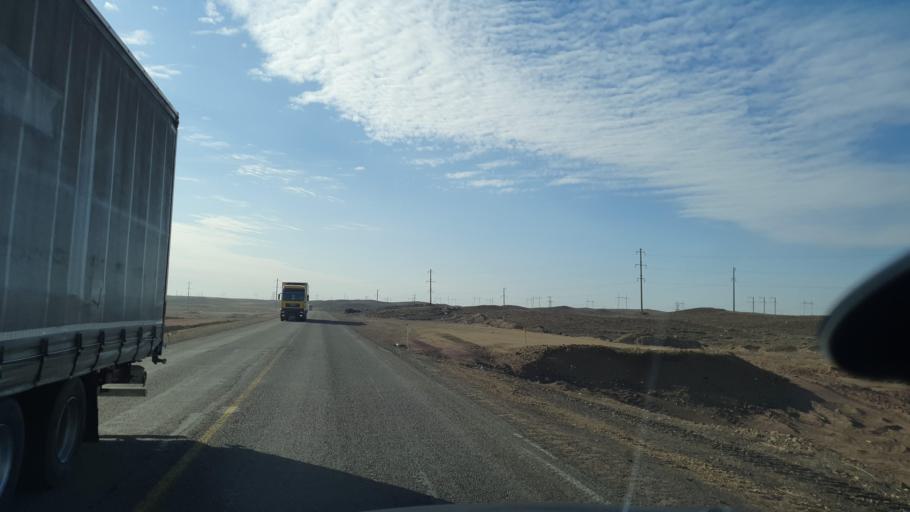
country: KZ
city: Priozersk
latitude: 45.8111
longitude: 73.4004
